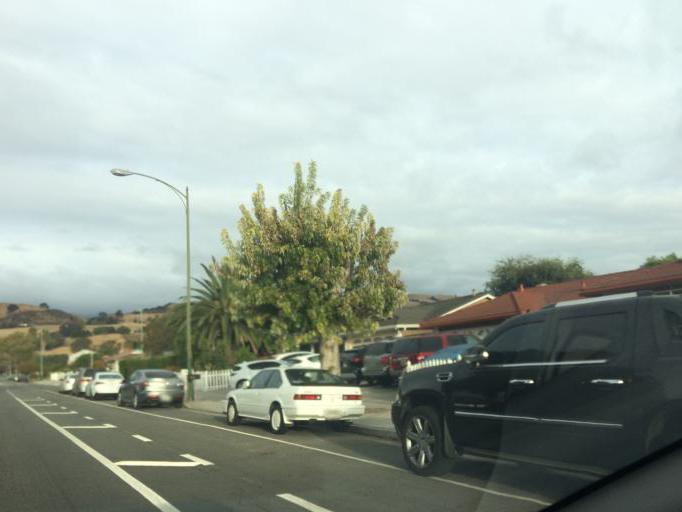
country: US
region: California
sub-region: Santa Clara County
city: Milpitas
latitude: 37.4142
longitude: -121.8596
